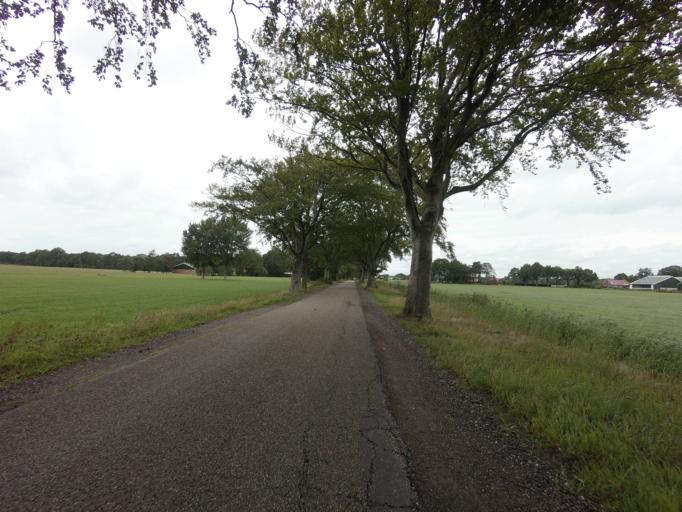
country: NL
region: Friesland
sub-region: Gemeente Weststellingwerf
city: Steggerda
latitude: 52.8795
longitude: 6.0910
